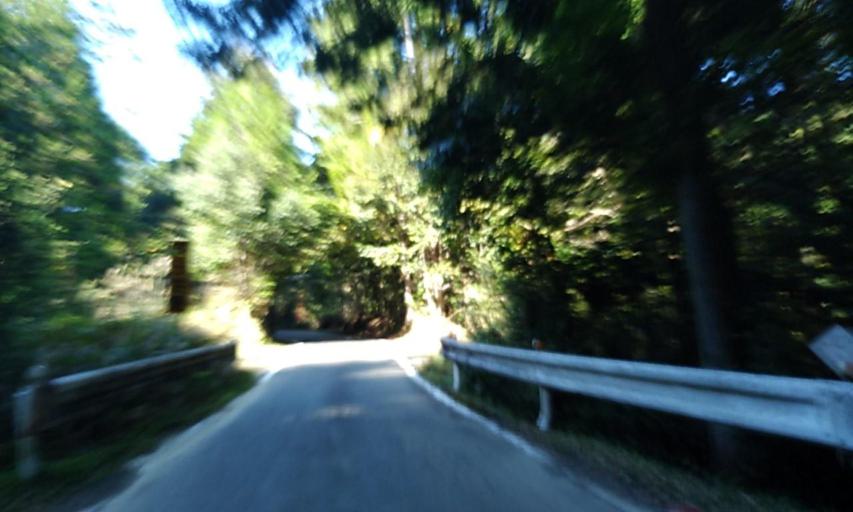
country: JP
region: Wakayama
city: Shingu
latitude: 33.9325
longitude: 135.9737
